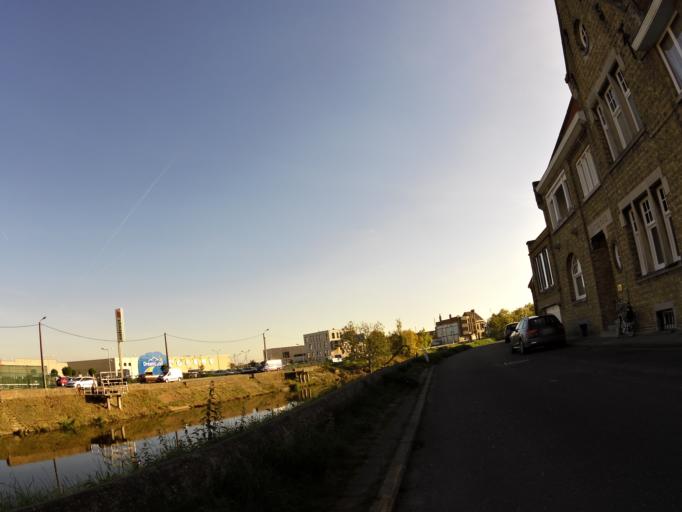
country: BE
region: Flanders
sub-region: Provincie West-Vlaanderen
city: Veurne
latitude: 51.0714
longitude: 2.6682
